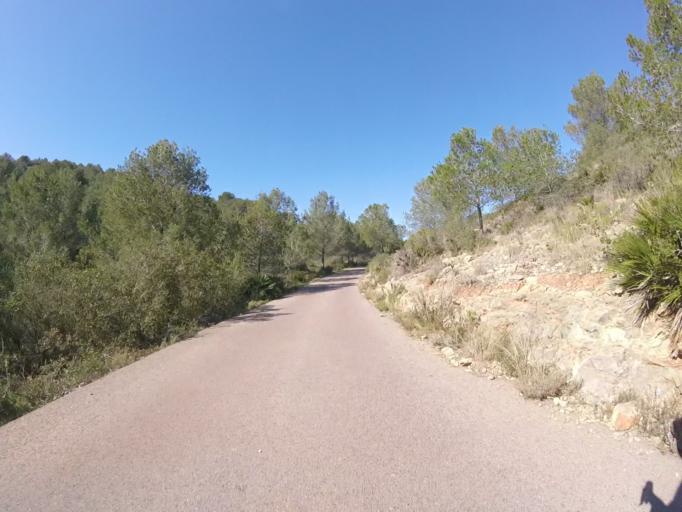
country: ES
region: Valencia
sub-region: Provincia de Castello
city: Benicassim
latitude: 40.0777
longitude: 0.0958
